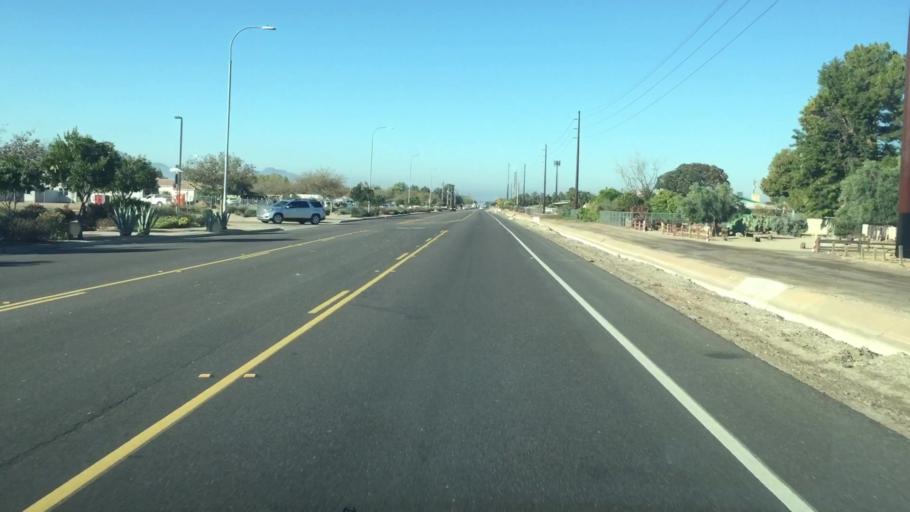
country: US
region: Arizona
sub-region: Maricopa County
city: Laveen
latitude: 33.3630
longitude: -112.1568
